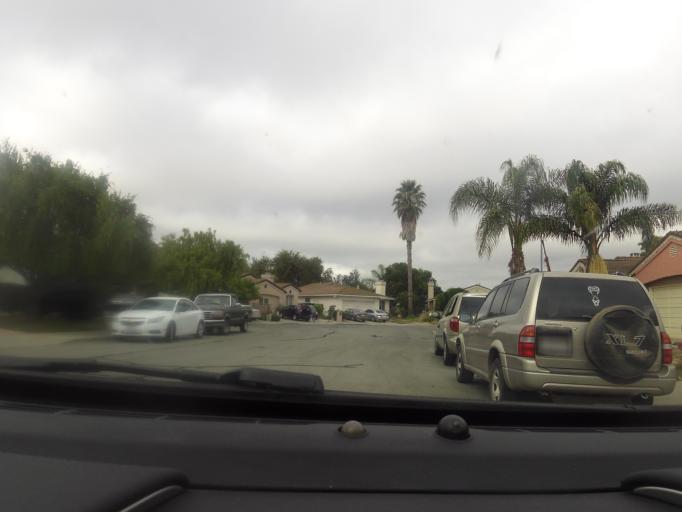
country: US
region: California
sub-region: San Benito County
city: Hollister
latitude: 36.8438
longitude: -121.4152
